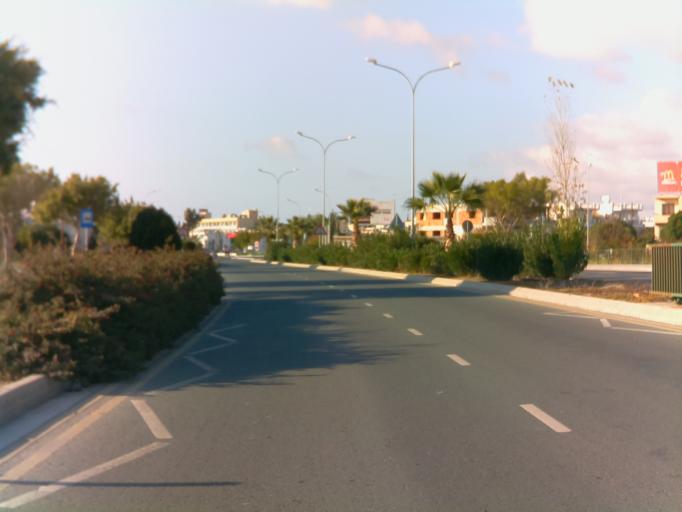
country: CY
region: Pafos
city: Paphos
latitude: 34.7579
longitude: 32.4239
